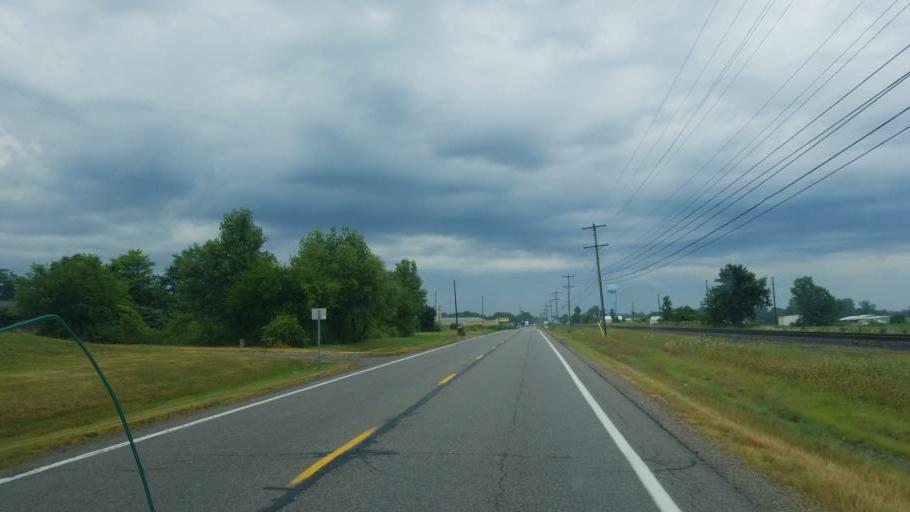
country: US
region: Ohio
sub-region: Williams County
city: Edgerton
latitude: 41.4451
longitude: -84.7653
